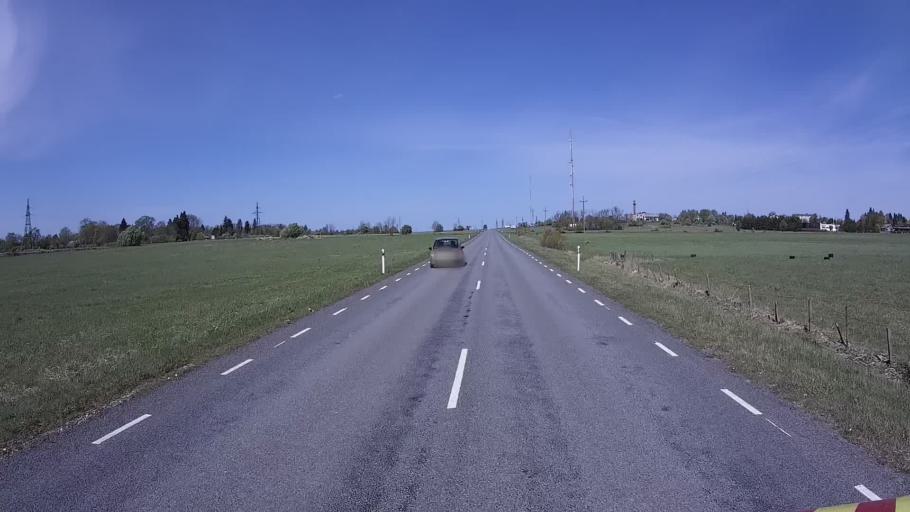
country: EE
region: Laeaene
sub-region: Lihula vald
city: Lihula
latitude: 58.6702
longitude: 23.8284
